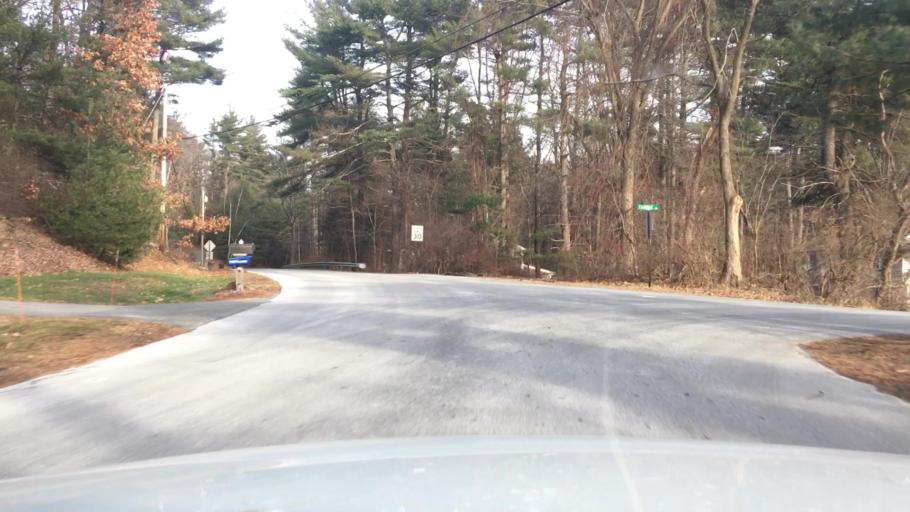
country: US
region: New Hampshire
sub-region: Rockingham County
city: Londonderry
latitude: 42.8843
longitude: -71.4181
